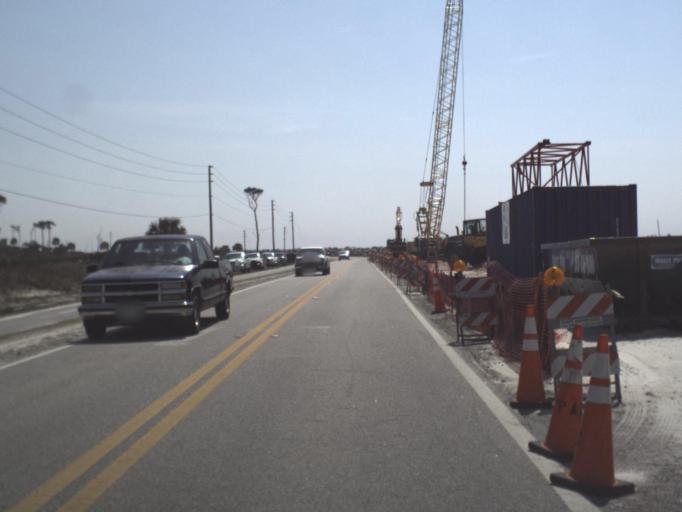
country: US
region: Florida
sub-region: Gulf County
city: Port Saint Joe
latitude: 29.6807
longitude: -85.3662
